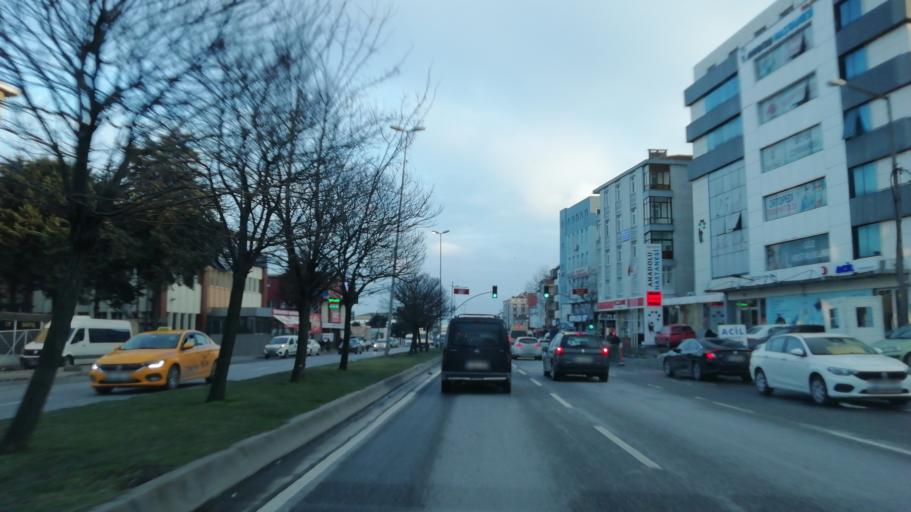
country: TR
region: Istanbul
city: Yakuplu
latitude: 41.0060
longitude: 28.7061
